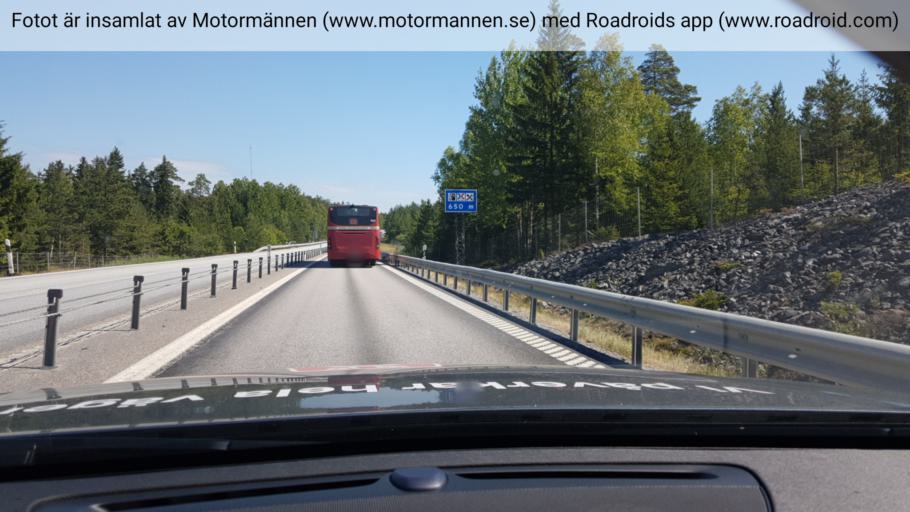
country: SE
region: Stockholm
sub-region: Norrtalje Kommun
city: Rimbo
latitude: 59.6267
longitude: 18.3123
